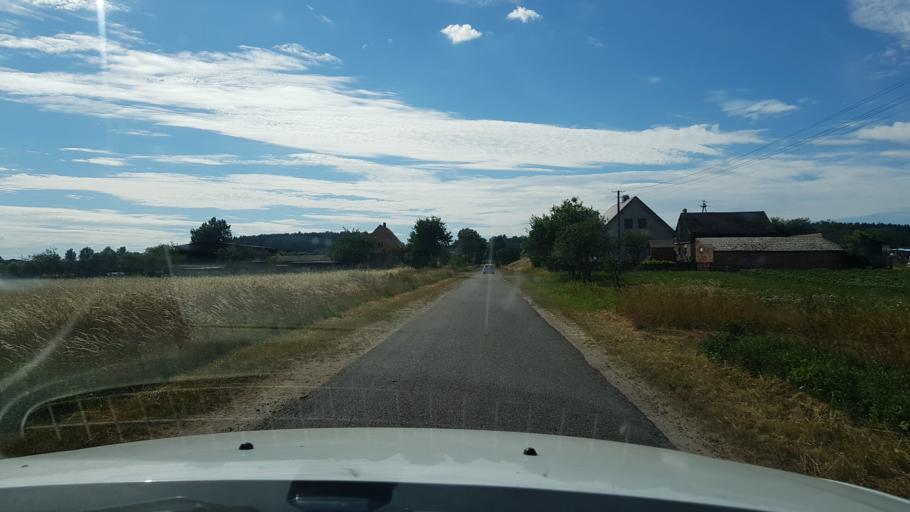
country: PL
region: West Pomeranian Voivodeship
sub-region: Powiat drawski
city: Zlocieniec
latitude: 53.6335
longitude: 16.0481
